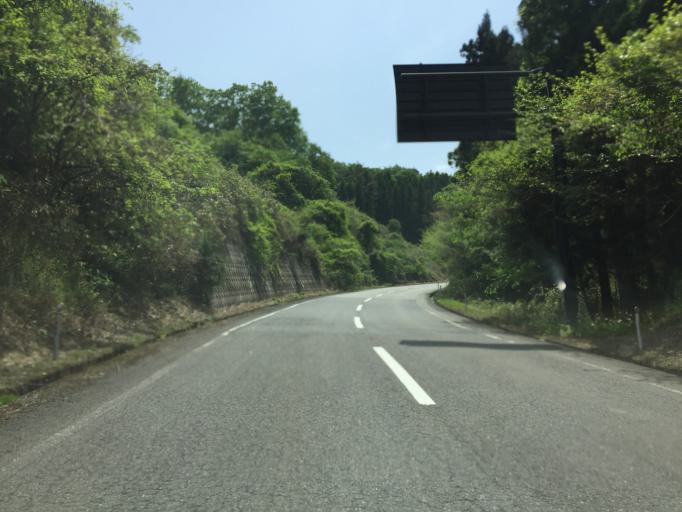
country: JP
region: Fukushima
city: Ishikawa
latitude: 37.1840
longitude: 140.5184
